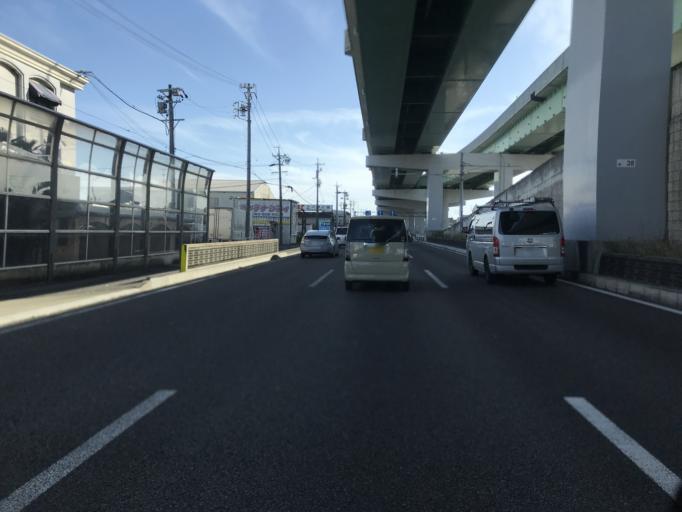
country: JP
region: Aichi
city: Iwakura
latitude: 35.2364
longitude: 136.8490
